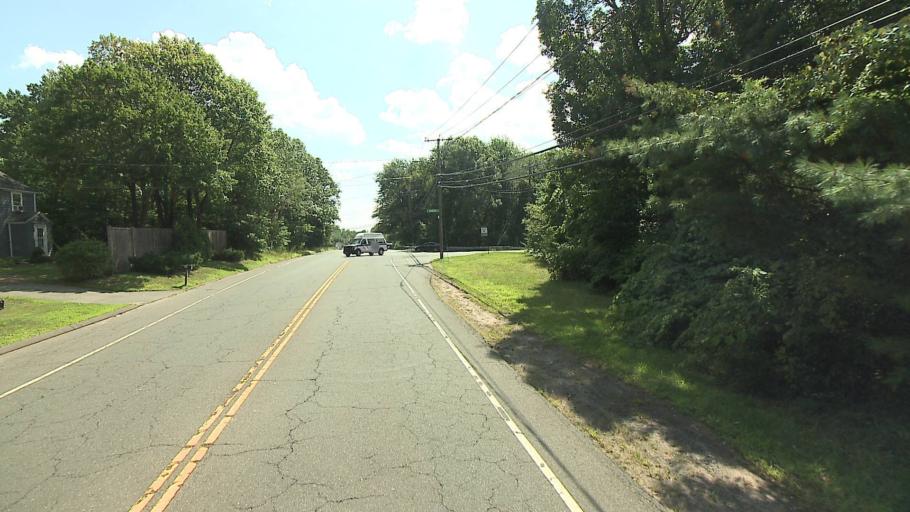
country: US
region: Connecticut
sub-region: Hartford County
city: Farmington
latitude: 41.7131
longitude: -72.8086
